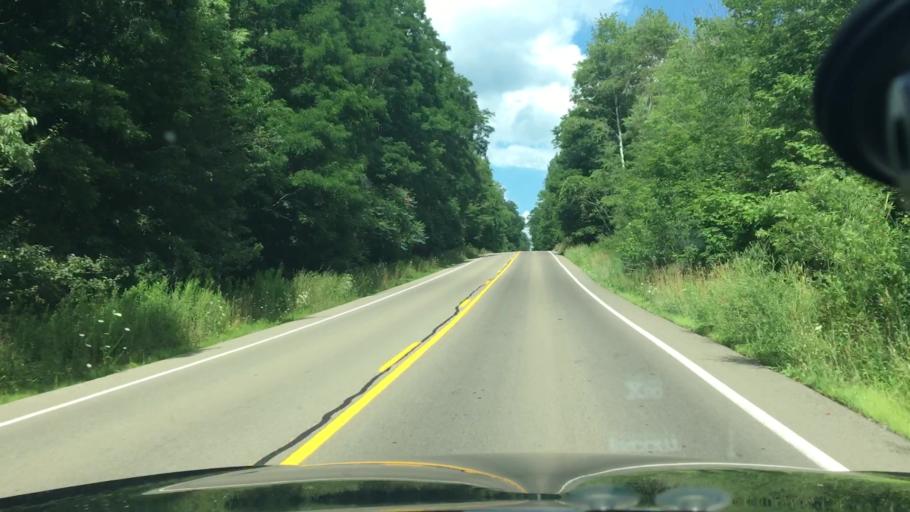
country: US
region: New York
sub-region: Chautauqua County
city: Lakewood
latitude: 42.1766
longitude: -79.3642
